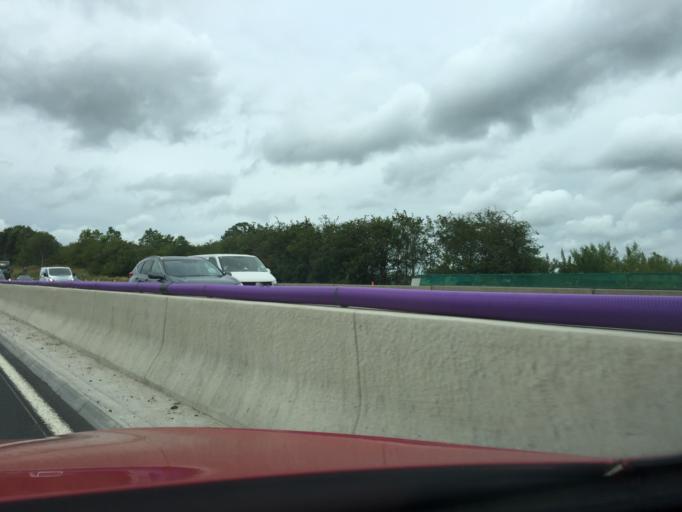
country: GB
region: England
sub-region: Milton Keynes
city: Gayhurst
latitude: 52.0956
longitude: -0.7608
